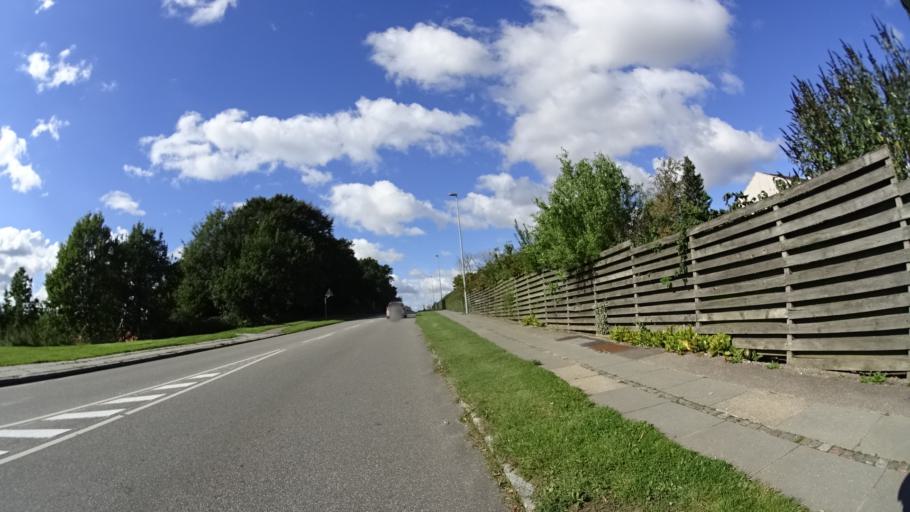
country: DK
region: Central Jutland
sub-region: Arhus Kommune
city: Arhus
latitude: 56.1139
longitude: 10.1898
